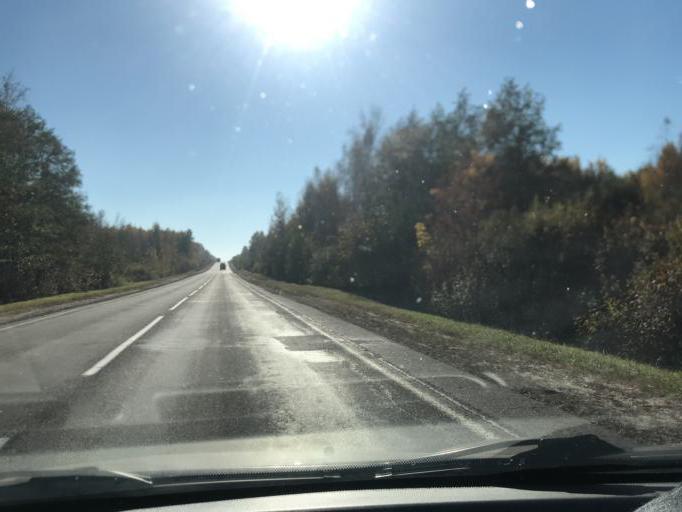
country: BY
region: Gomel
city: Kastsyukowka
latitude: 52.4242
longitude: 30.8283
